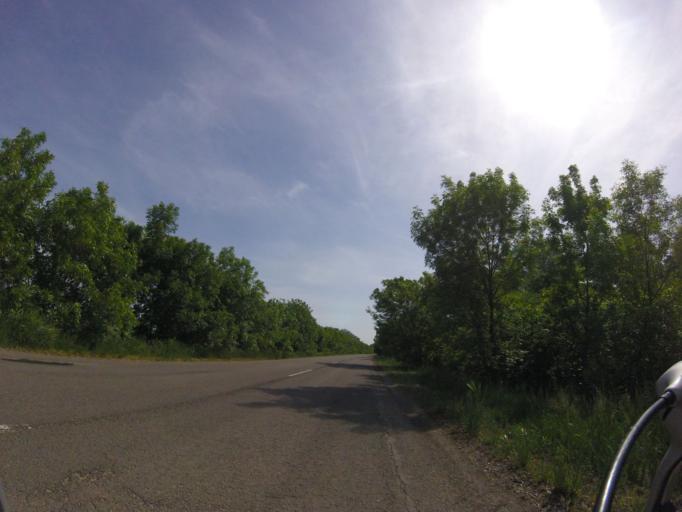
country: HU
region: Jasz-Nagykun-Szolnok
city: Tiszapuspoki
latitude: 47.2539
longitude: 20.3017
